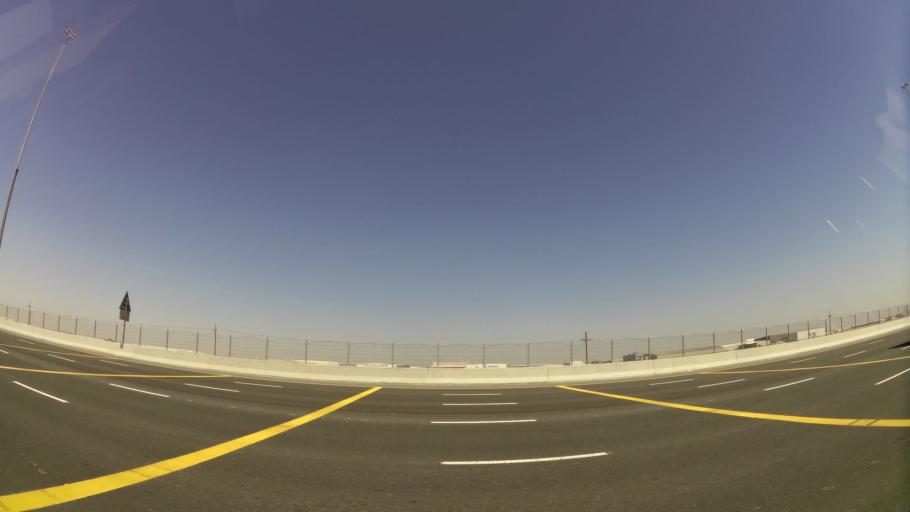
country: AE
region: Dubai
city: Dubai
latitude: 24.9654
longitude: 55.1395
